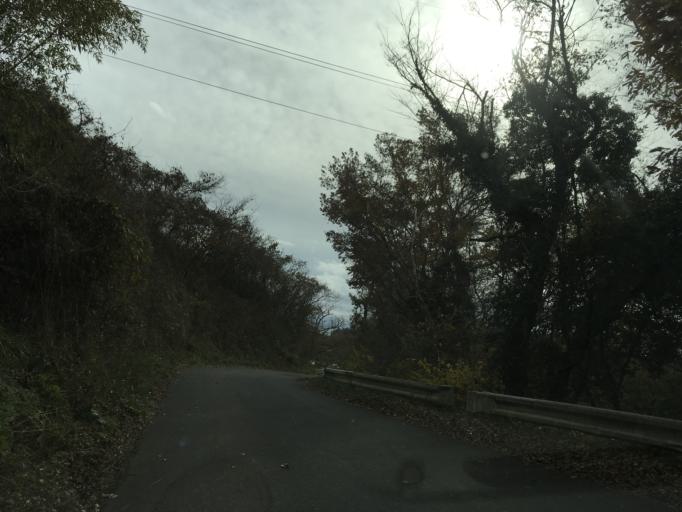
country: JP
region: Iwate
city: Ichinoseki
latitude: 38.7621
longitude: 141.2752
